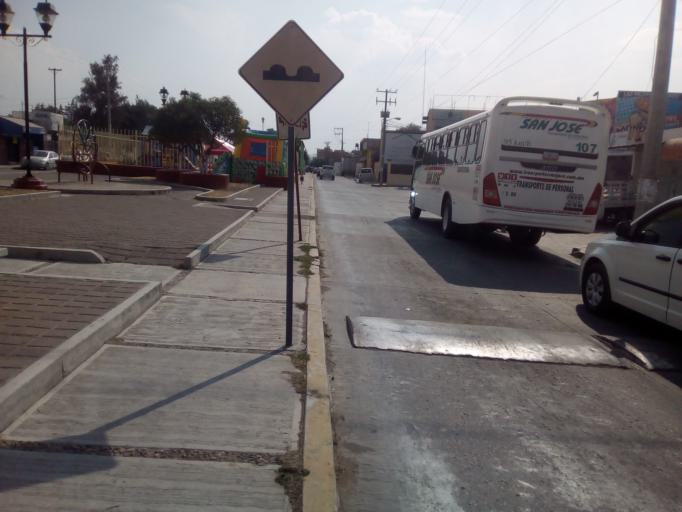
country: MX
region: Guerrero
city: San Luis de la Paz
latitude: 21.2916
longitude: -100.5153
